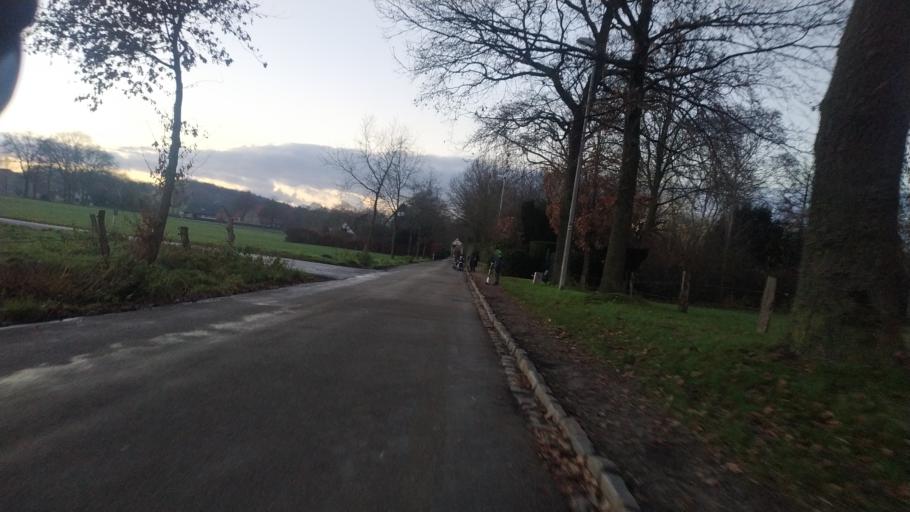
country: DE
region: North Rhine-Westphalia
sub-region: Regierungsbezirk Munster
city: Mettingen
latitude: 52.3181
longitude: 7.7692
